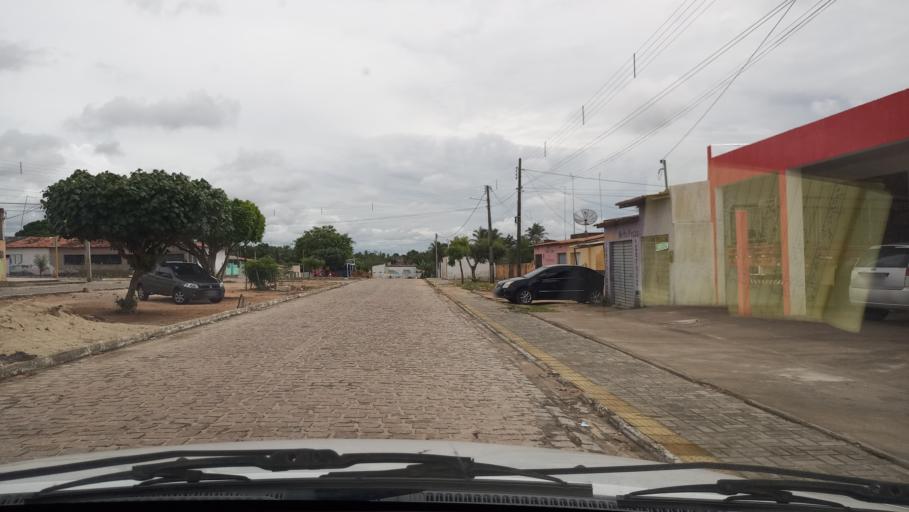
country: BR
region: Rio Grande do Norte
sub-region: Poco Branco
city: Poco Branco
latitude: -5.6186
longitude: -35.6583
